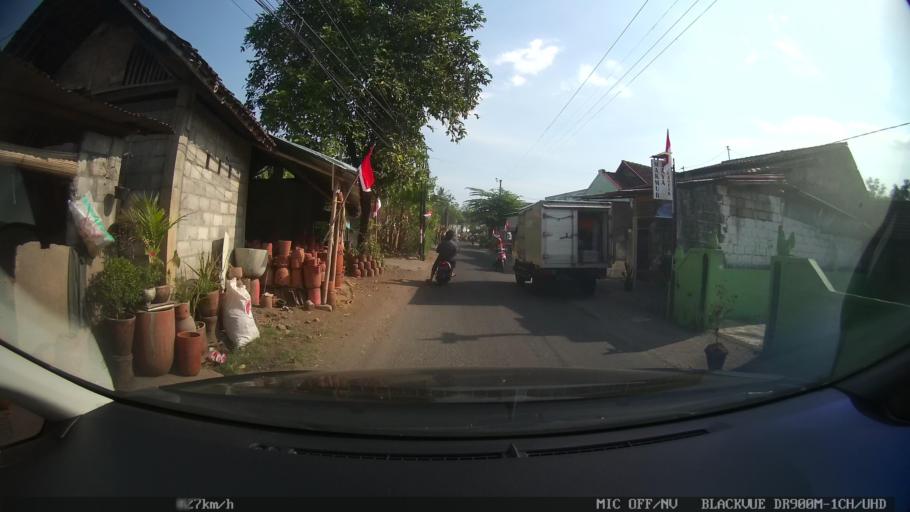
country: ID
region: Daerah Istimewa Yogyakarta
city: Kasihan
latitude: -7.8413
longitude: 110.3330
